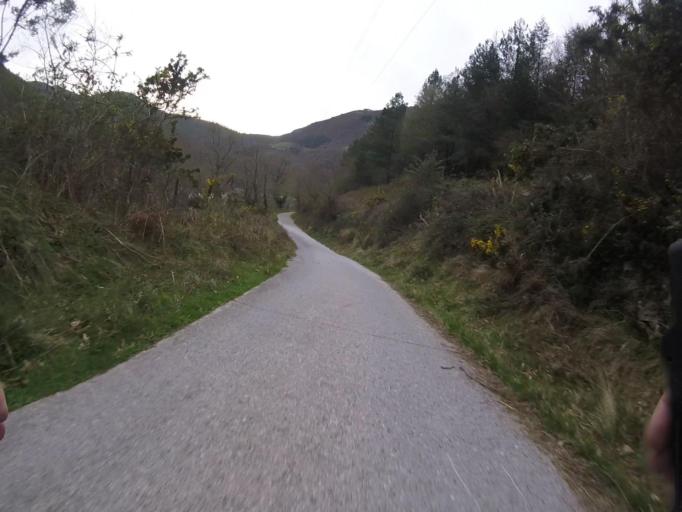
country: ES
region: Basque Country
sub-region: Provincia de Guipuzcoa
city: Irun
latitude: 43.2747
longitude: -1.7659
